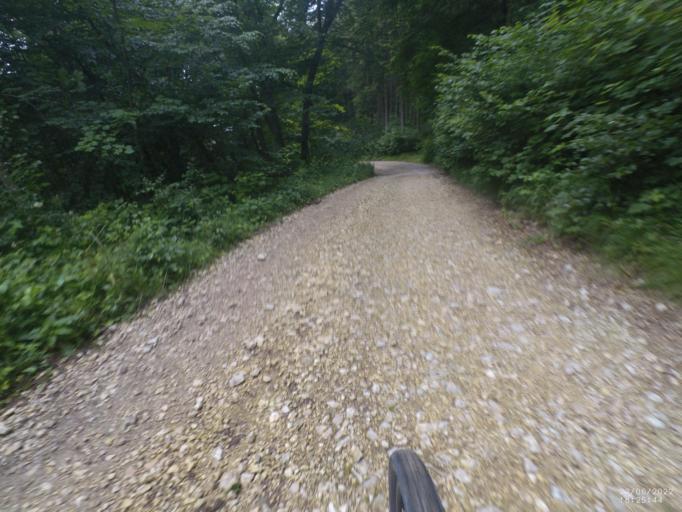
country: DE
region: Baden-Wuerttemberg
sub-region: Regierungsbezirk Stuttgart
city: Gerstetten
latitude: 48.6176
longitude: 9.9662
